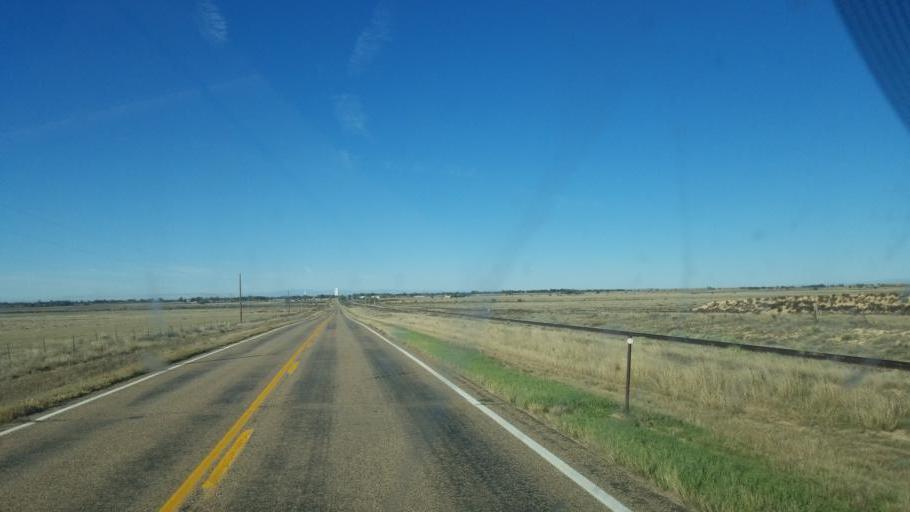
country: US
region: Colorado
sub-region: Crowley County
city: Ordway
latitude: 38.2421
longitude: -103.6220
